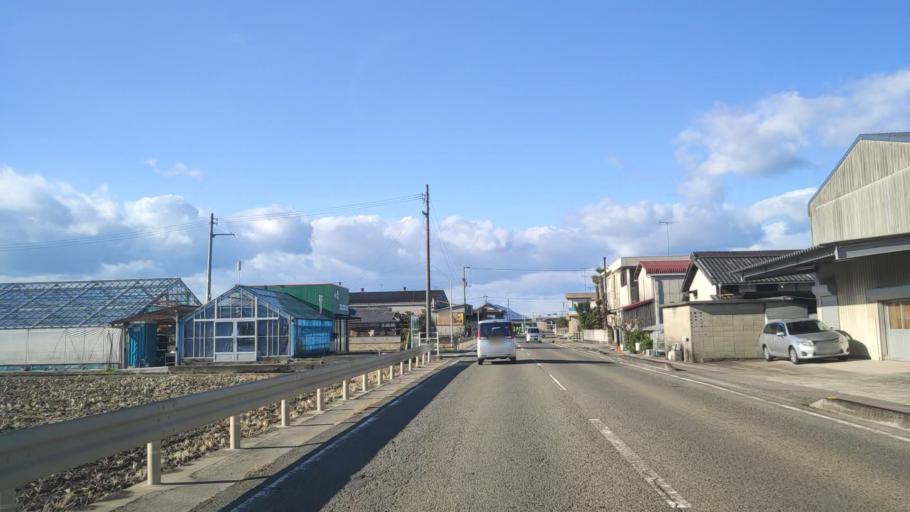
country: JP
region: Ehime
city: Saijo
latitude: 33.9148
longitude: 133.1064
